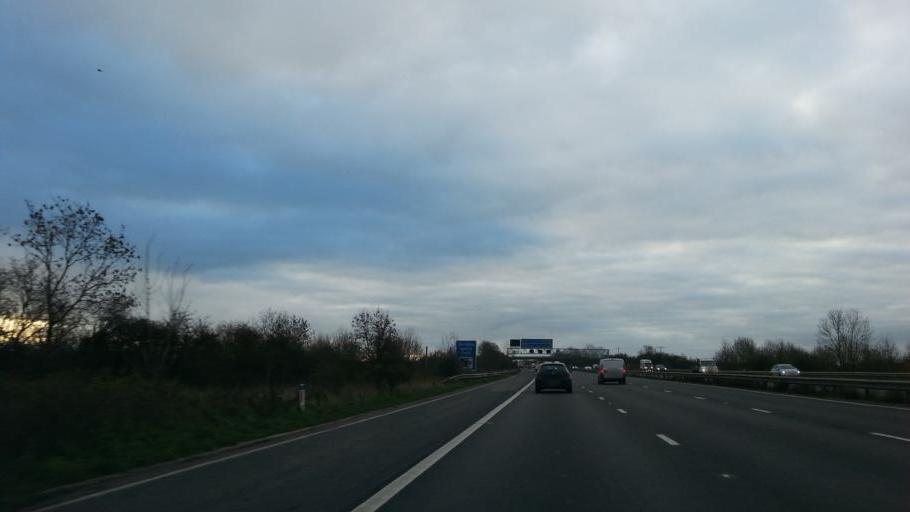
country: GB
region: England
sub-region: Leicestershire
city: Lutterworth
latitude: 52.4260
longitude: -1.1911
